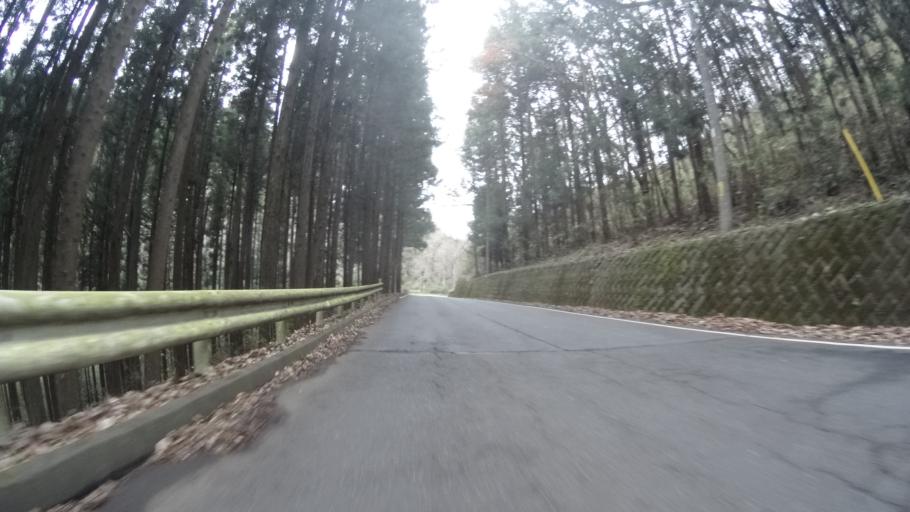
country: JP
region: Yamanashi
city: Uenohara
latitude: 35.6379
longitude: 139.1264
